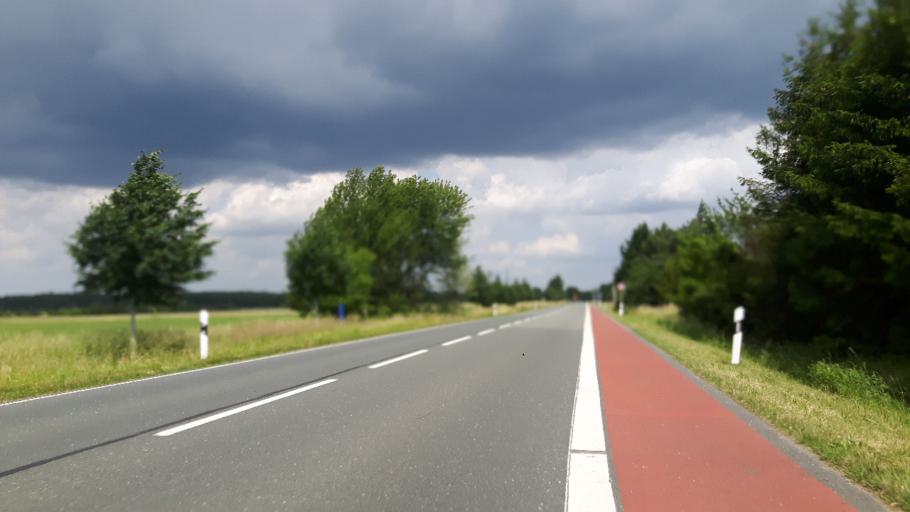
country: DE
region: Saxony-Anhalt
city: Schlaitz
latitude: 51.6840
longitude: 12.4471
